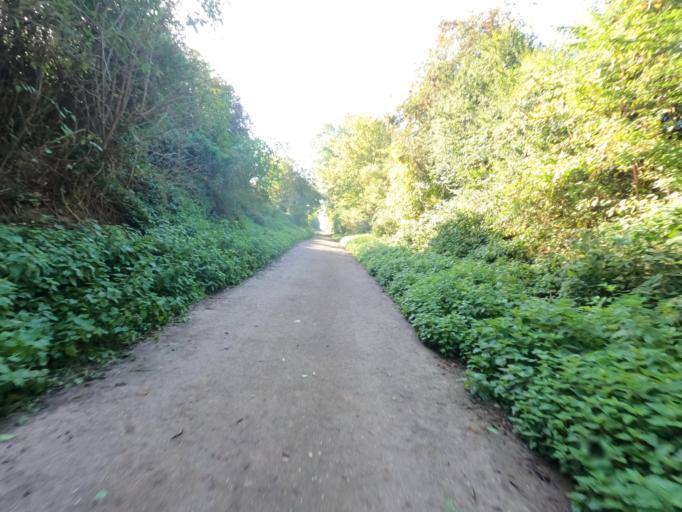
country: DE
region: North Rhine-Westphalia
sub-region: Regierungsbezirk Koln
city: Linnich
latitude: 50.9955
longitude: 6.2408
